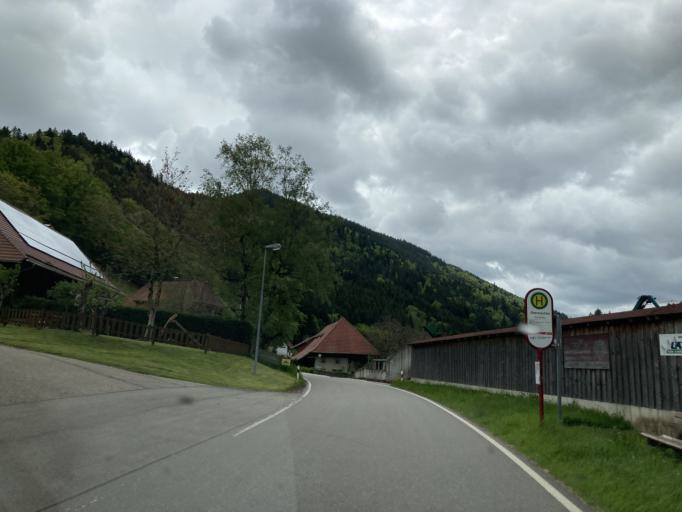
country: DE
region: Baden-Wuerttemberg
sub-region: Freiburg Region
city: Schonach im Schwarzwald
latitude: 48.1887
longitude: 8.1597
